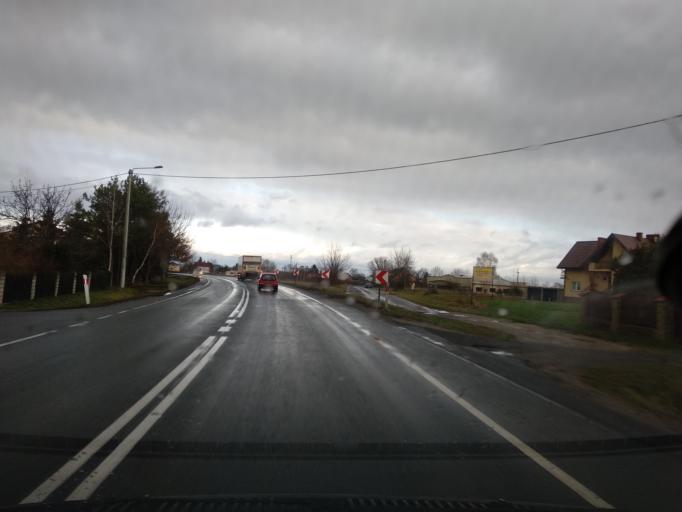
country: PL
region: Greater Poland Voivodeship
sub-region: Powiat koninski
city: Stare Miasto
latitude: 52.1524
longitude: 18.2046
